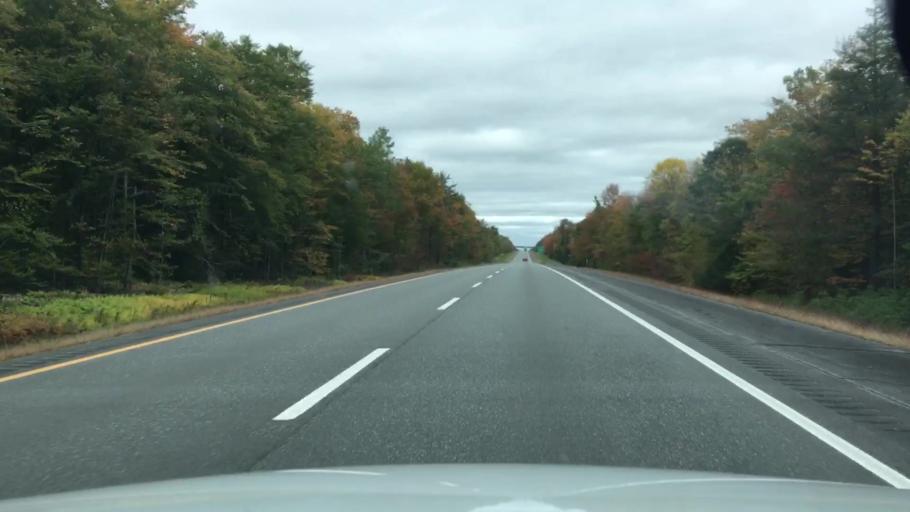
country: US
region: Maine
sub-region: Waldo County
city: Burnham
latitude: 44.7263
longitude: -69.4385
